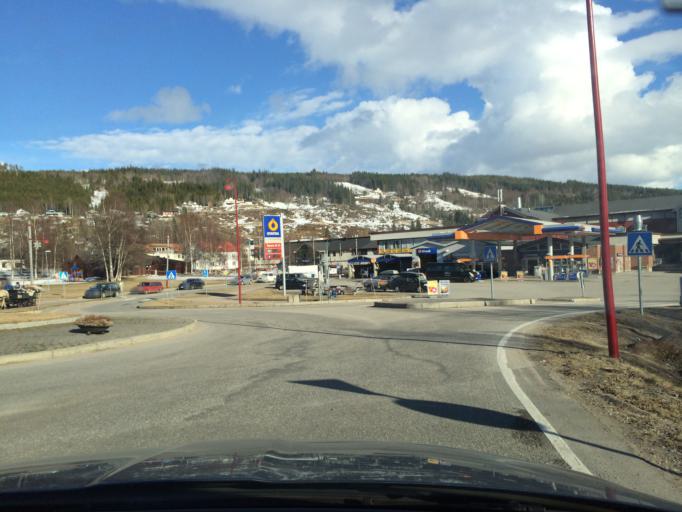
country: NO
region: Hedmark
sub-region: Trysil
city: Innbygda
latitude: 61.3162
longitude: 12.2597
